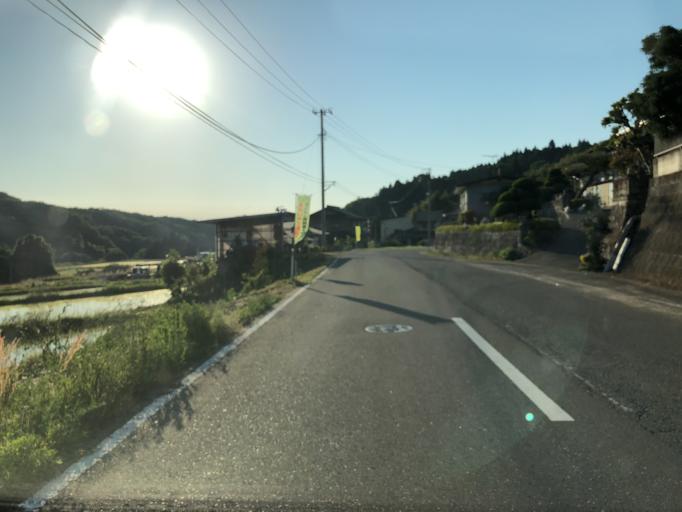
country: JP
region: Fukushima
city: Ishikawa
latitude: 37.0432
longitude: 140.4351
